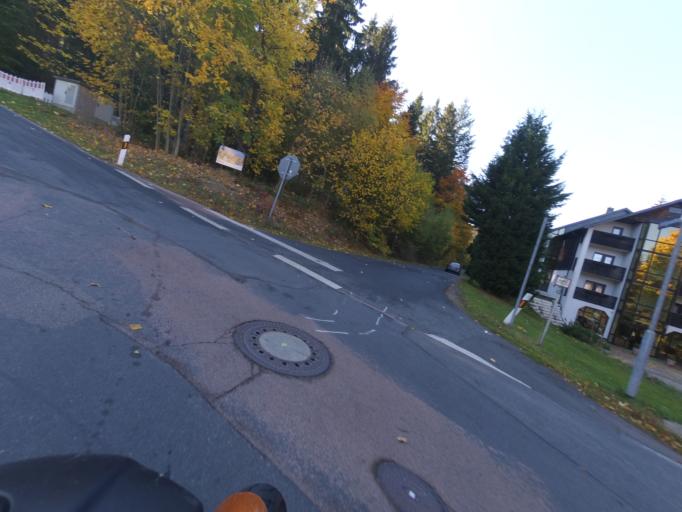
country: DE
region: Saxony
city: Altenberg
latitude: 50.7895
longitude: 13.7439
